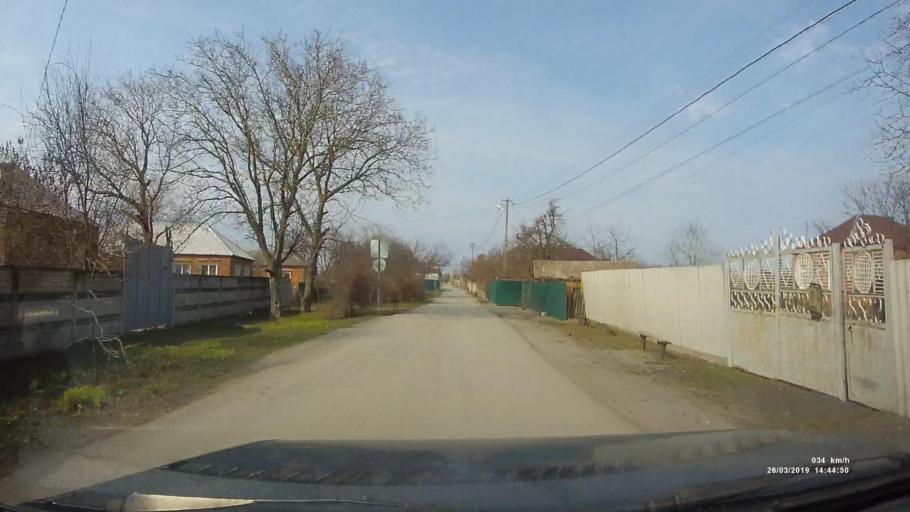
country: RU
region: Rostov
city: Novobessergenovka
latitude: 47.1795
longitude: 38.8626
